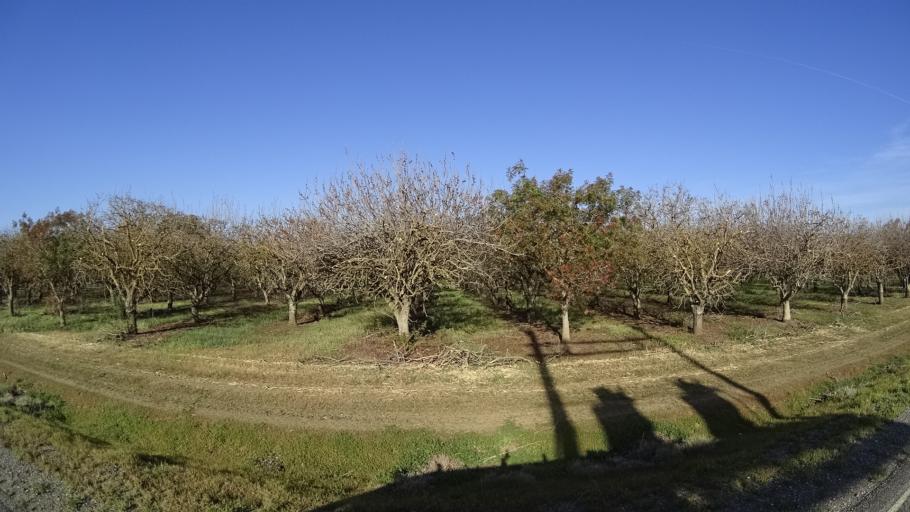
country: US
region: California
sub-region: Glenn County
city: Willows
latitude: 39.5211
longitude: -122.2268
